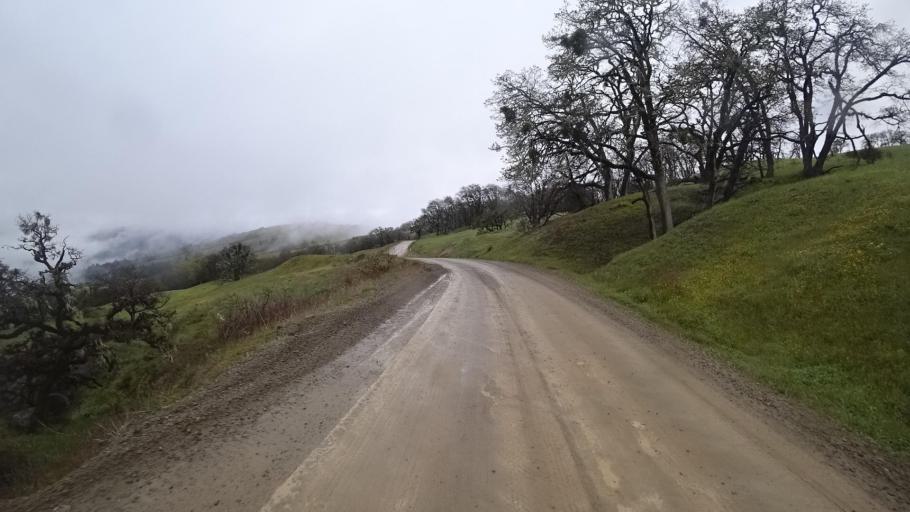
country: US
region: California
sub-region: Humboldt County
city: Westhaven-Moonstone
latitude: 41.1470
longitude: -123.8802
